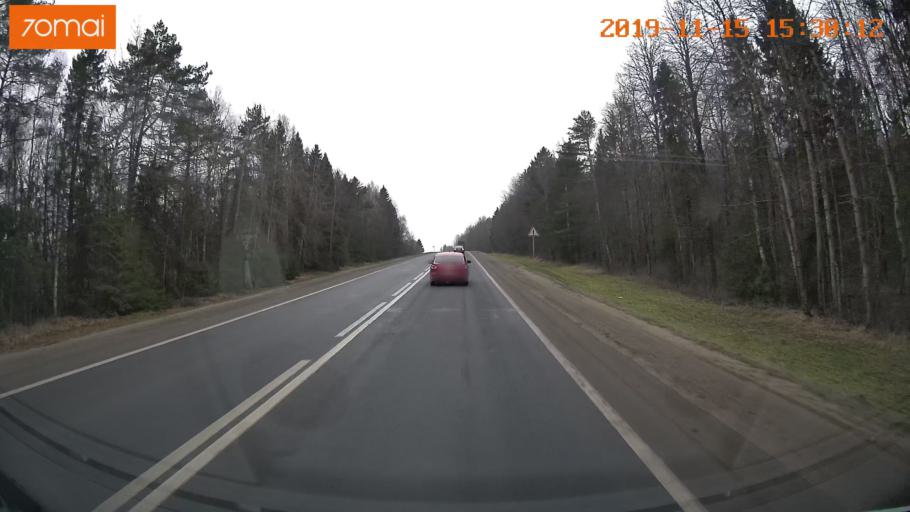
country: RU
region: Jaroslavl
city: Danilov
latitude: 58.1124
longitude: 40.1145
